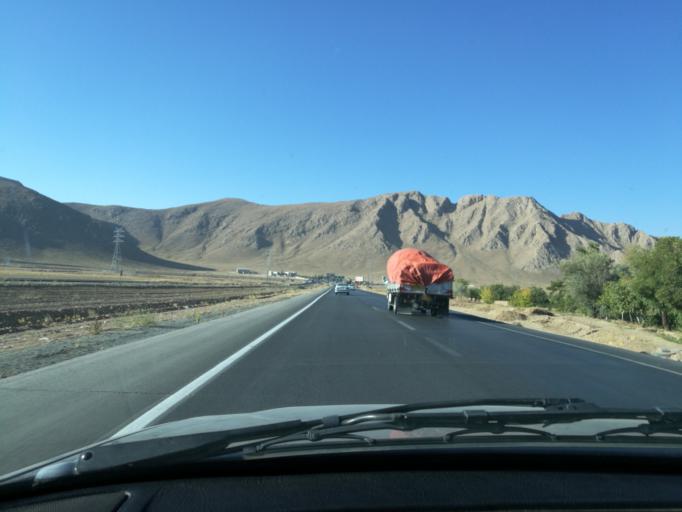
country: IR
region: Chahar Mahall va Bakhtiari
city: Farrokh Shahr
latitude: 32.2898
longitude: 51.0179
